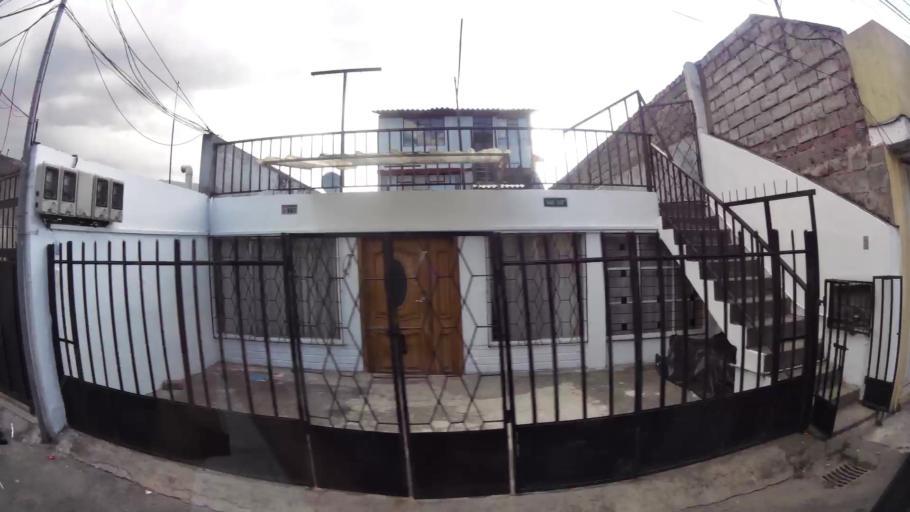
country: EC
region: Pichincha
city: Quito
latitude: -0.1242
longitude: -78.4870
